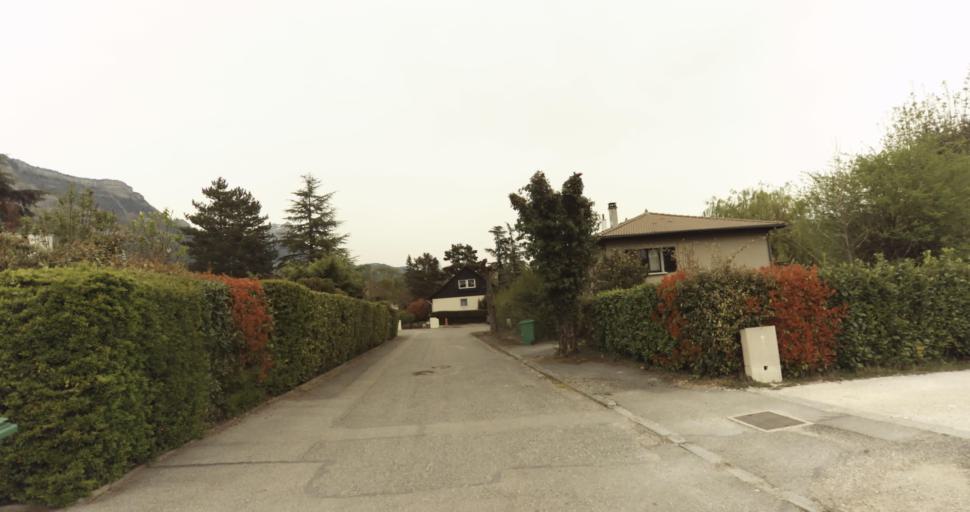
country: FR
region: Rhone-Alpes
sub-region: Departement de l'Isere
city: Biviers
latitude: 45.2303
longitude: 5.8045
